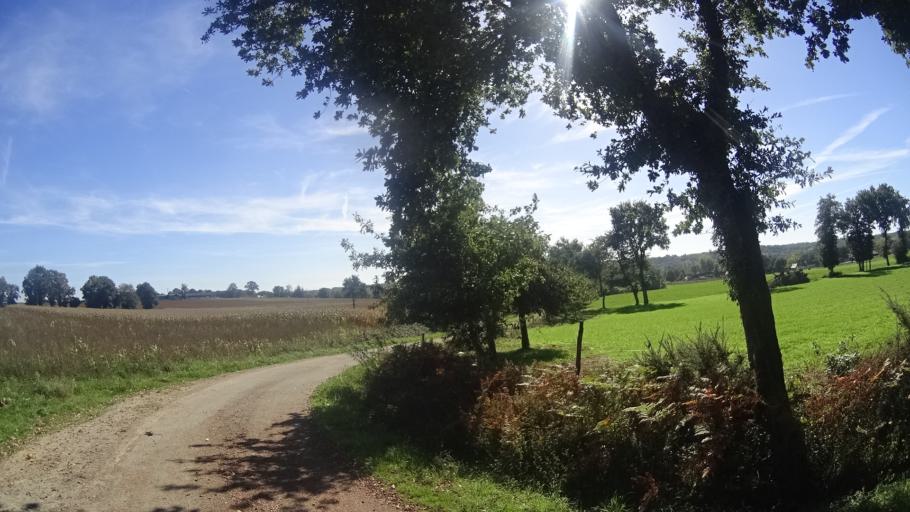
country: FR
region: Brittany
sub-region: Departement du Morbihan
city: Peillac
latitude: 47.7368
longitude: -2.1788
